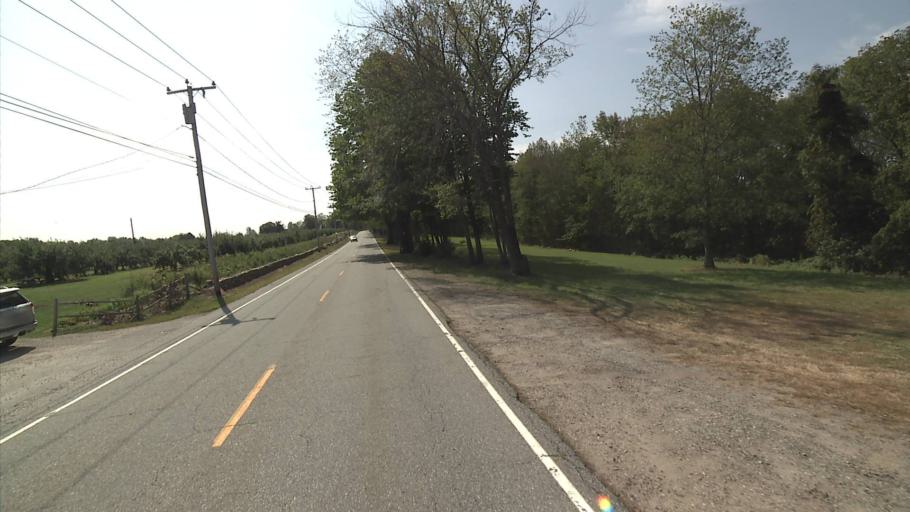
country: US
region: Connecticut
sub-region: Windham County
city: East Brooklyn
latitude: 41.8306
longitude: -71.9588
